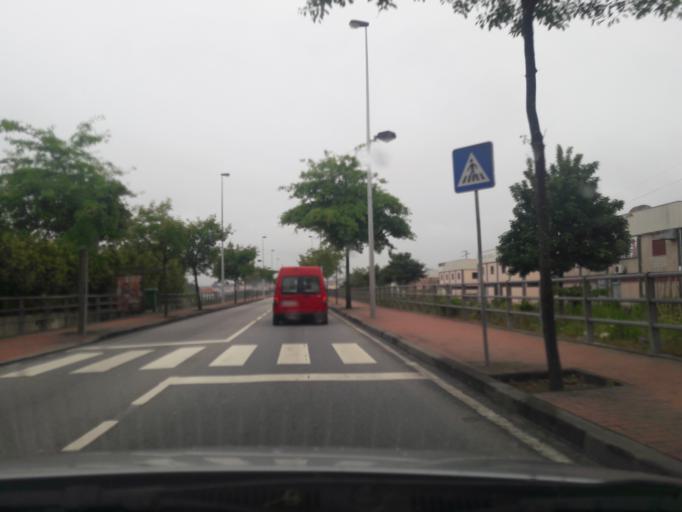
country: PT
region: Porto
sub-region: Vila do Conde
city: Arvore
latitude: 41.3315
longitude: -8.7199
